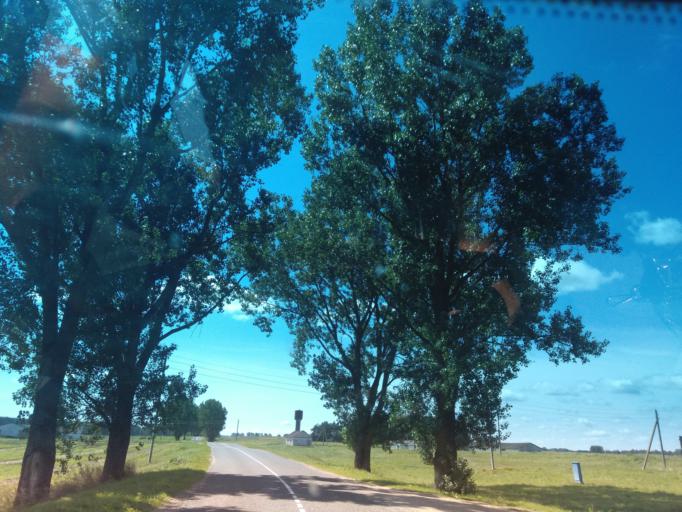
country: BY
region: Minsk
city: Uzda
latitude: 53.2859
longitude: 27.2323
